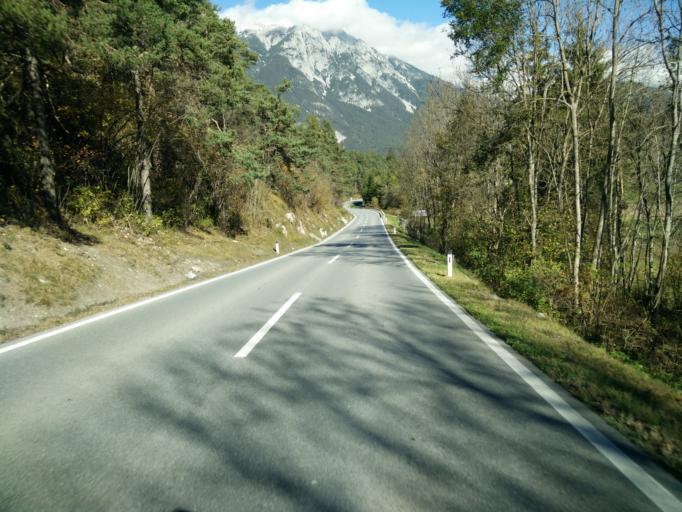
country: AT
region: Tyrol
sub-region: Politischer Bezirk Imst
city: Nassereith
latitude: 47.2960
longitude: 10.8303
